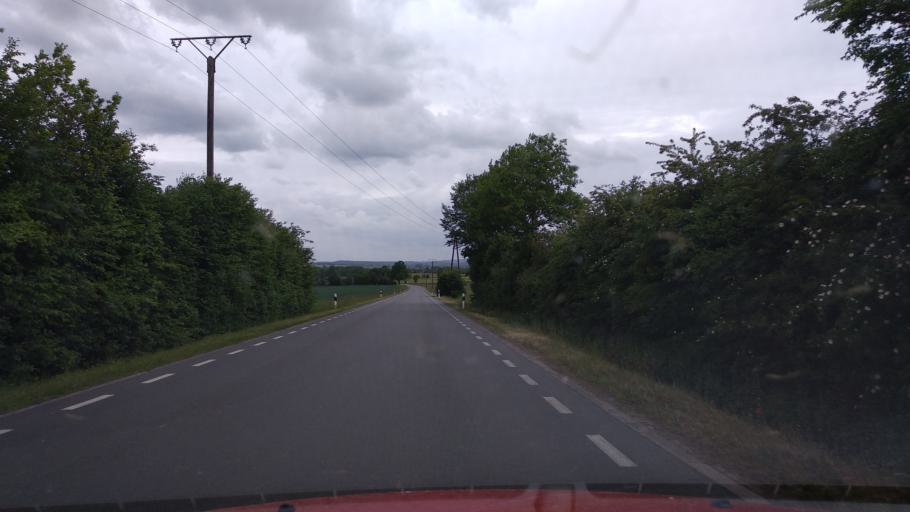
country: DE
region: North Rhine-Westphalia
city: Borgentreich
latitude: 51.5430
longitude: 9.2346
